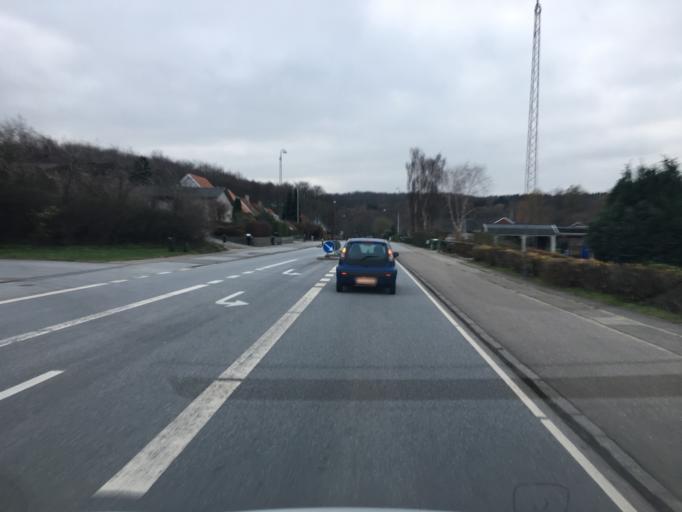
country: DK
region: South Denmark
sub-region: Aabenraa Kommune
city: Aabenraa
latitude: 55.0330
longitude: 9.3838
